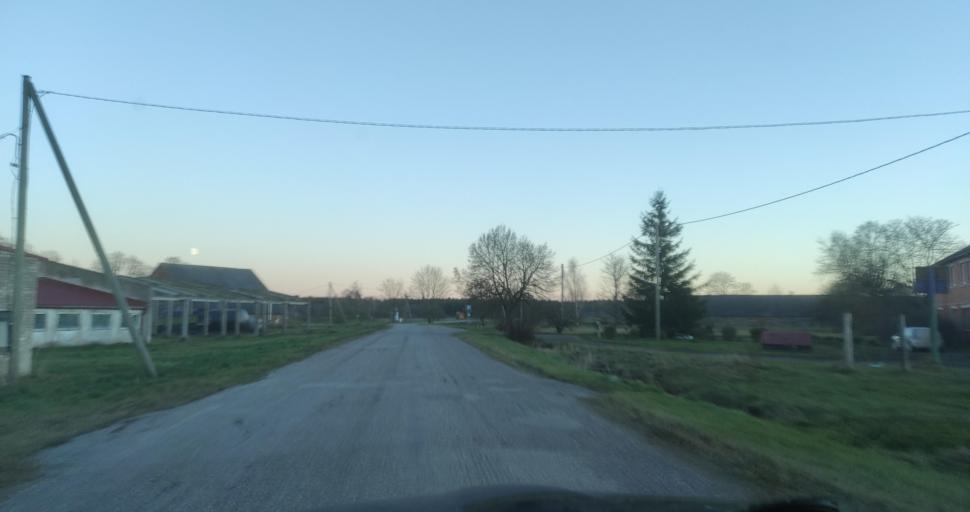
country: LV
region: Dundaga
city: Dundaga
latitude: 57.3762
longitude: 22.2275
